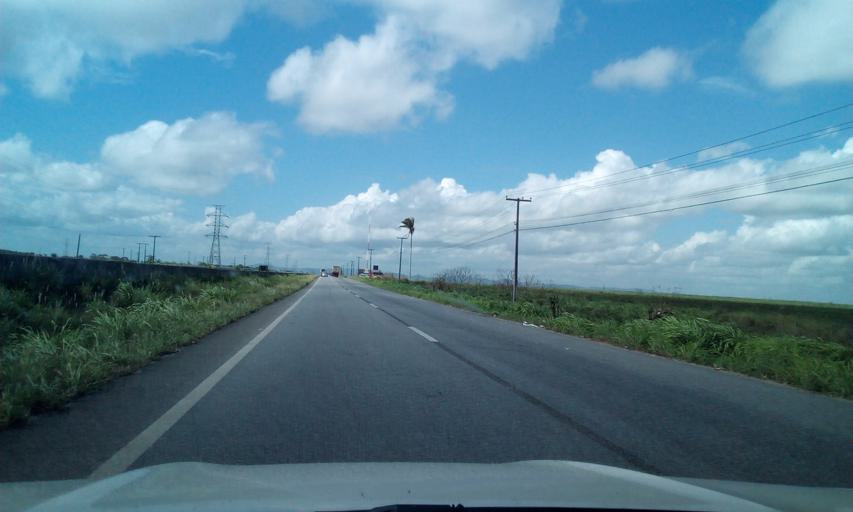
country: BR
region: Alagoas
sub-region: Messias
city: Messias
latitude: -9.4285
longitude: -35.8380
